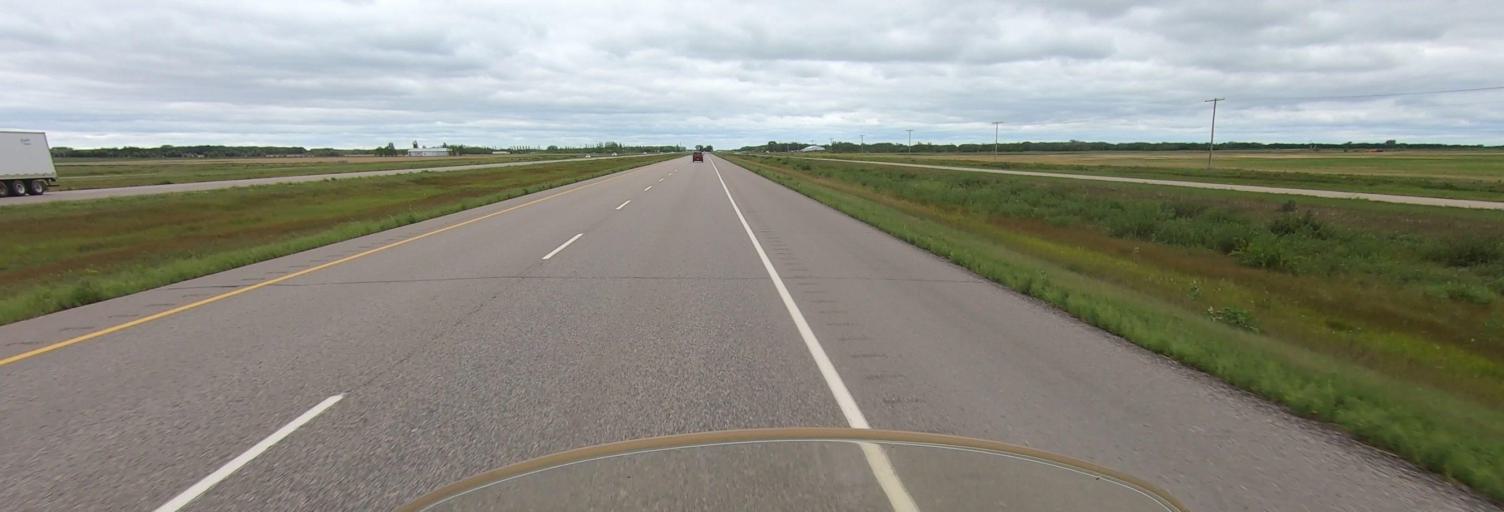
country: CA
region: Manitoba
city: Portage la Prairie
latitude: 49.9751
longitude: -98.6415
